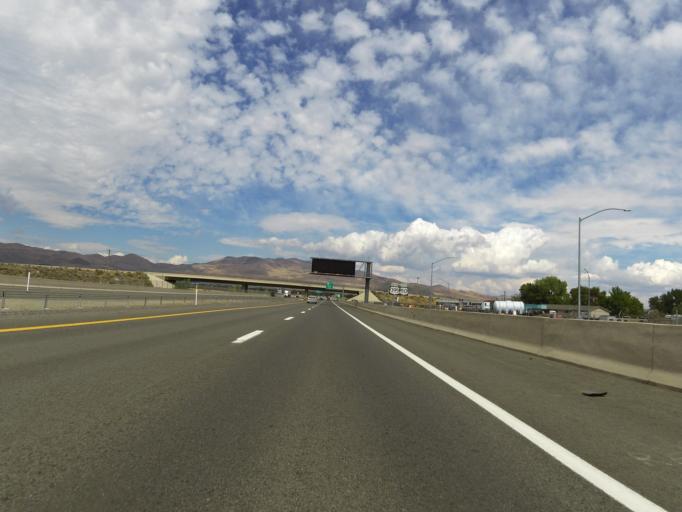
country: US
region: Nevada
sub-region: Carson City
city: Carson City
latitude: 39.1594
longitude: -119.7415
